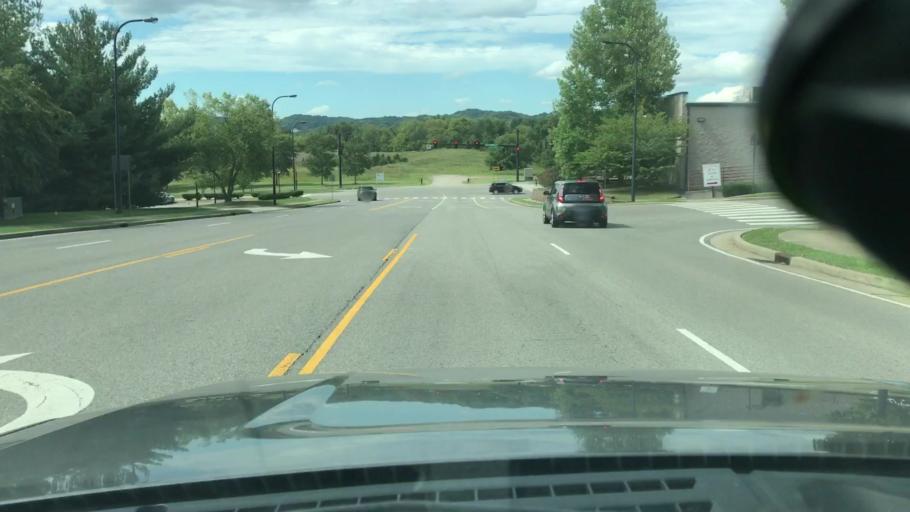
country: US
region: Tennessee
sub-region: Williamson County
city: Franklin
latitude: 35.9398
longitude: -86.8309
